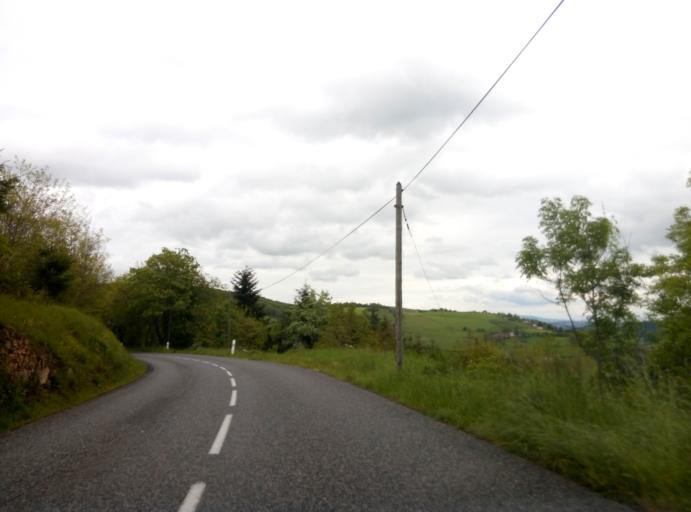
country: FR
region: Rhone-Alpes
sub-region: Departement du Rhone
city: Tarare
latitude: 45.9357
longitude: 4.4298
